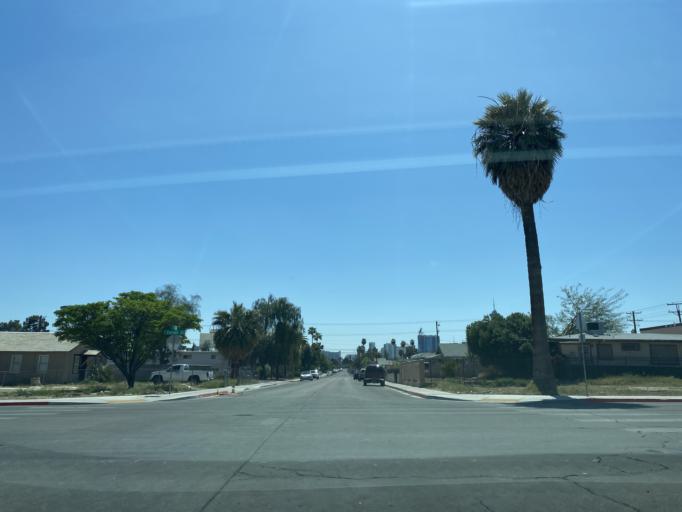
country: US
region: Nevada
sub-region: Clark County
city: Las Vegas
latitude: 36.1652
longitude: -115.1345
